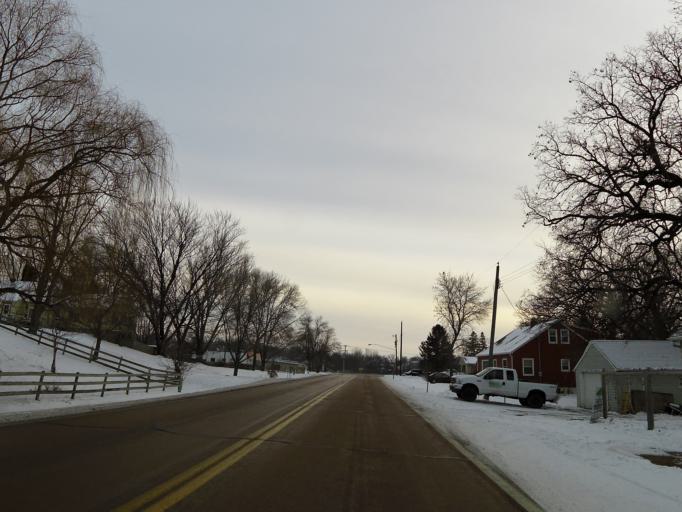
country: US
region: Minnesota
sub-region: Carver County
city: Victoria
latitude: 44.8632
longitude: -93.6717
